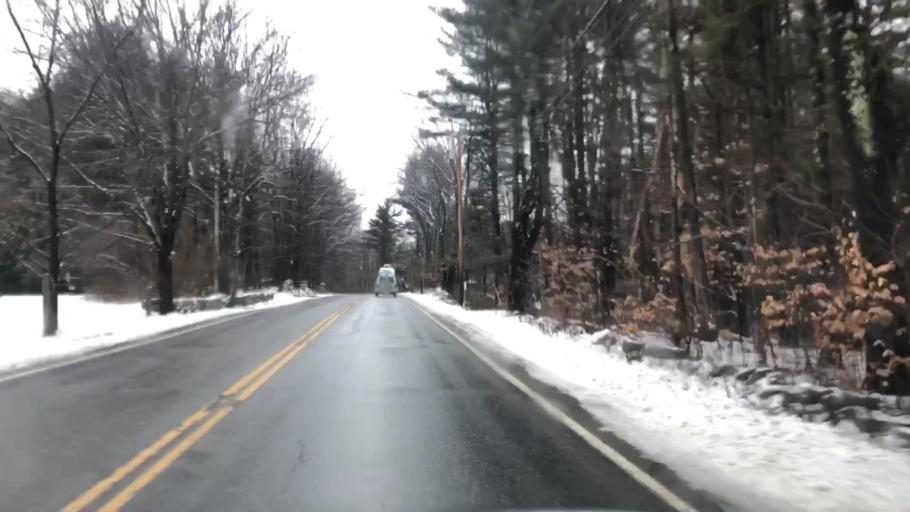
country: US
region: New Hampshire
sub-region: Hillsborough County
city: Weare
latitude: 43.0415
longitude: -71.7051
